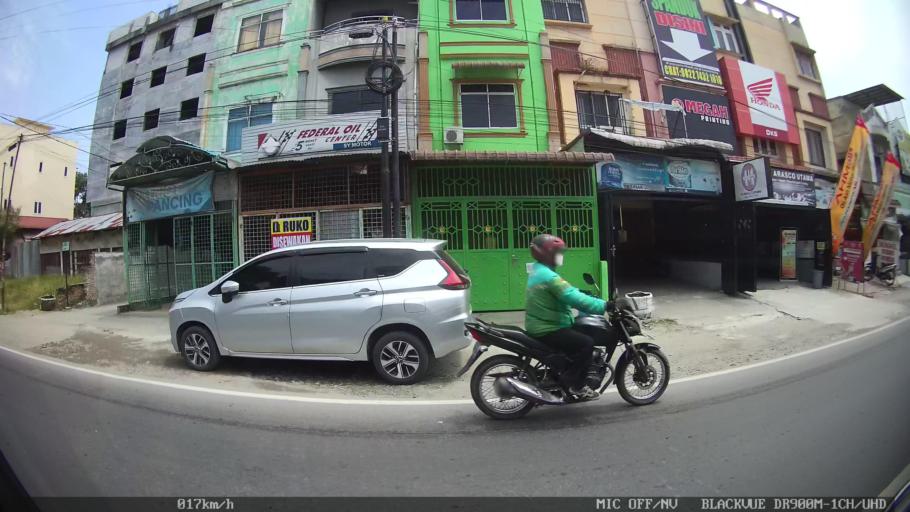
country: ID
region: North Sumatra
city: Sunggal
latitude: 3.5857
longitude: 98.6212
